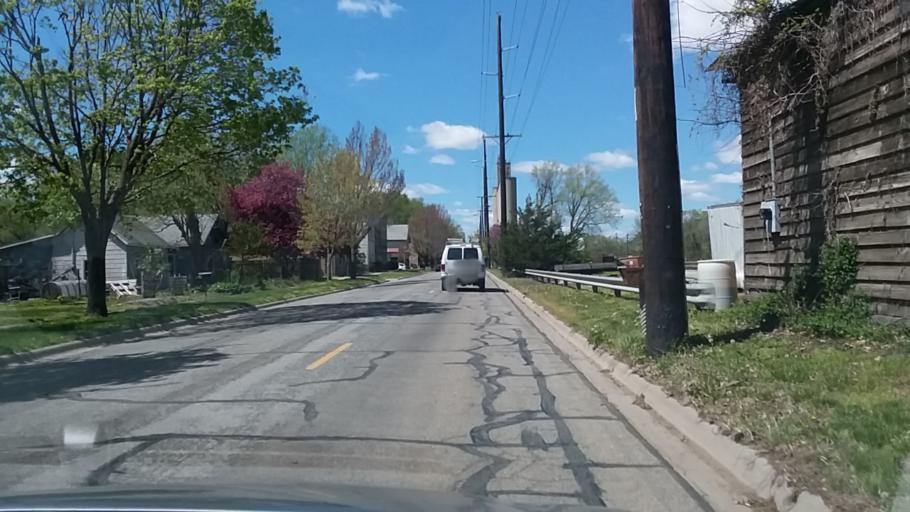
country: US
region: Kansas
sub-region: Douglas County
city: Lawrence
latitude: 38.9778
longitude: -95.2274
